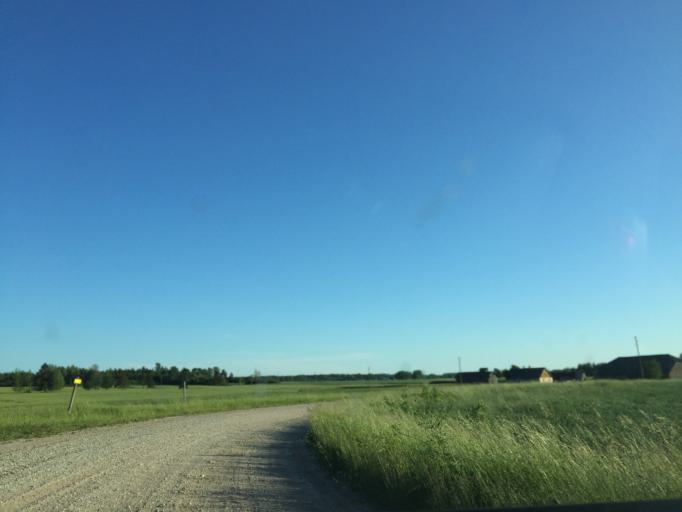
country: LV
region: Broceni
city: Broceni
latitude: 56.8647
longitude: 22.6055
